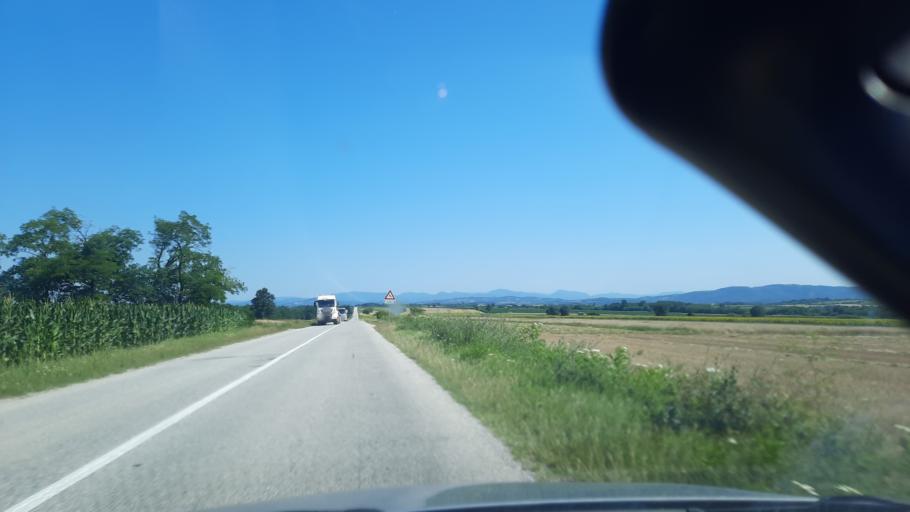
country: RS
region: Central Serbia
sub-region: Branicevski Okrug
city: Malo Crnice
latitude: 44.5763
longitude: 21.4216
